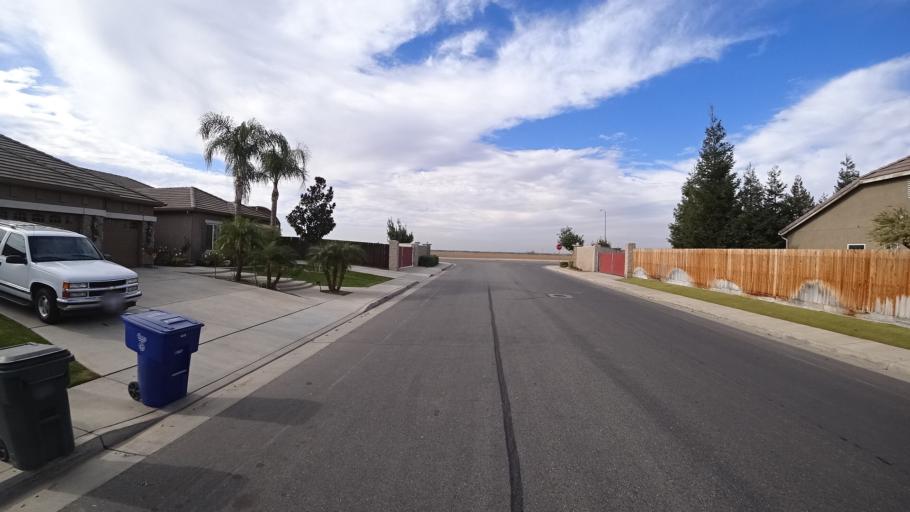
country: US
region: California
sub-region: Kern County
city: Rosedale
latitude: 35.4245
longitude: -119.1448
